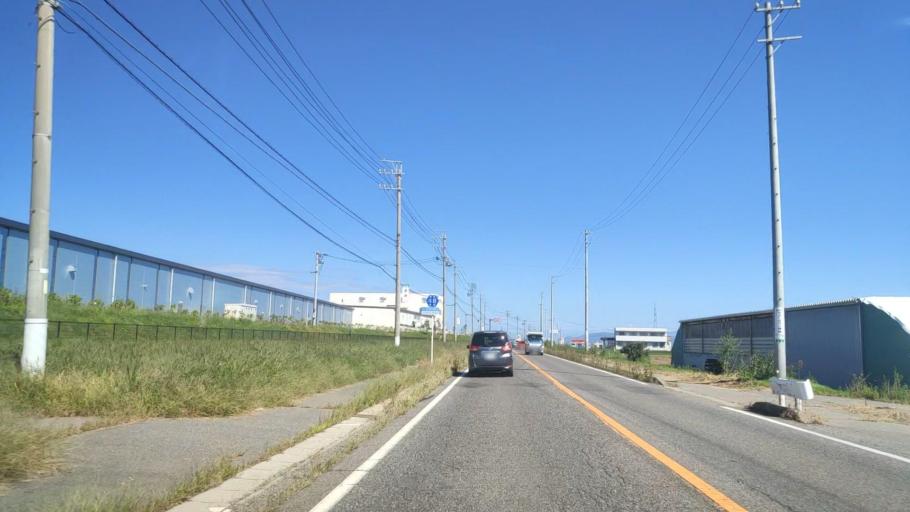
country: JP
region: Nagano
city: Matsumoto
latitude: 36.1911
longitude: 137.9031
